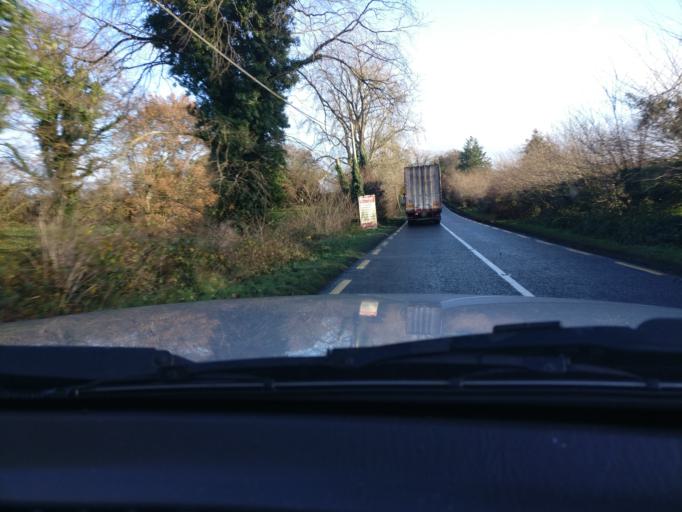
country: IE
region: Leinster
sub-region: An Mhi
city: Athboy
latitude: 53.6663
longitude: -6.9944
